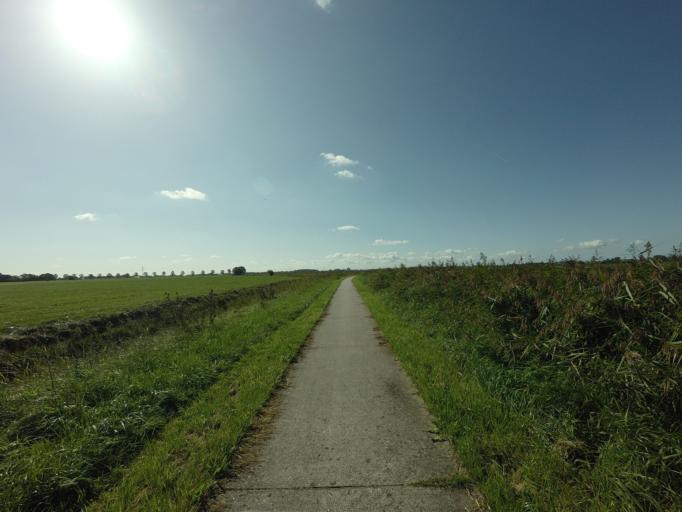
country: NL
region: Friesland
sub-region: Gemeente Boarnsterhim
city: Reduzum
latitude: 53.1255
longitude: 5.7550
